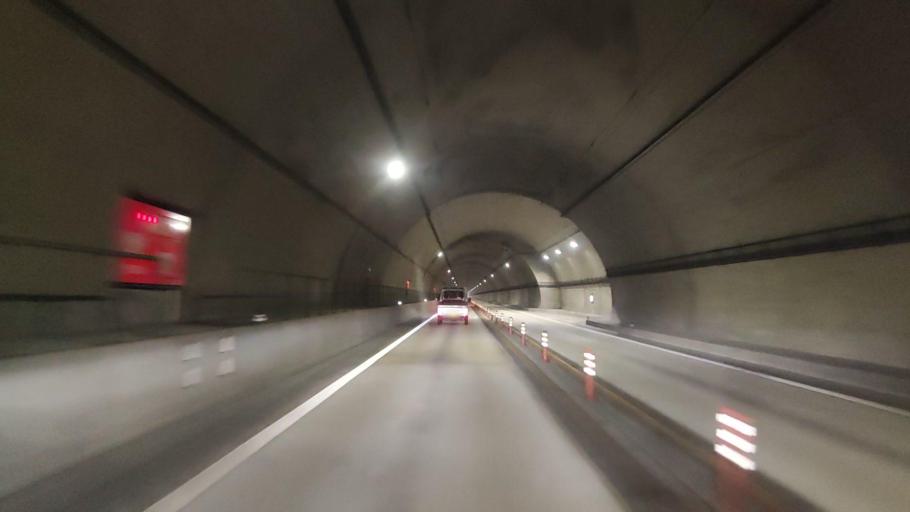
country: JP
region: Wakayama
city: Tanabe
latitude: 33.6224
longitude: 135.4191
